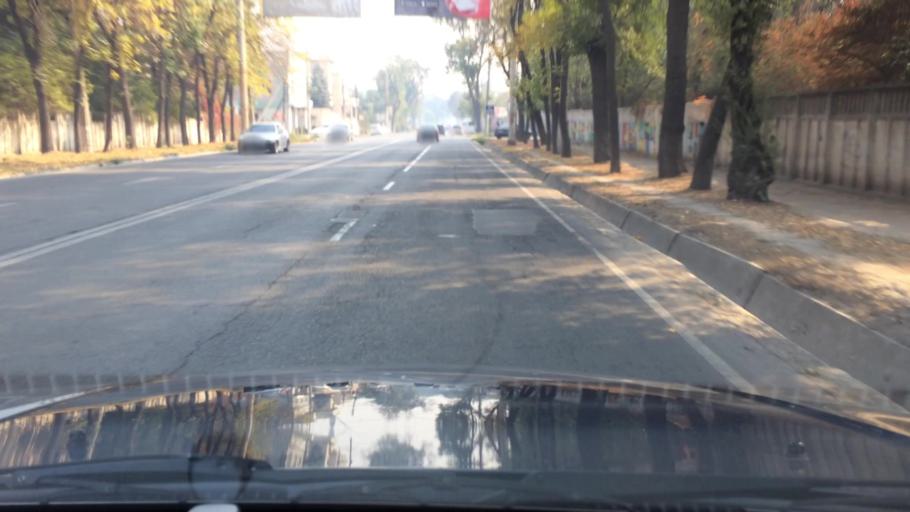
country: KG
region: Chuy
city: Bishkek
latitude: 42.8575
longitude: 74.5913
